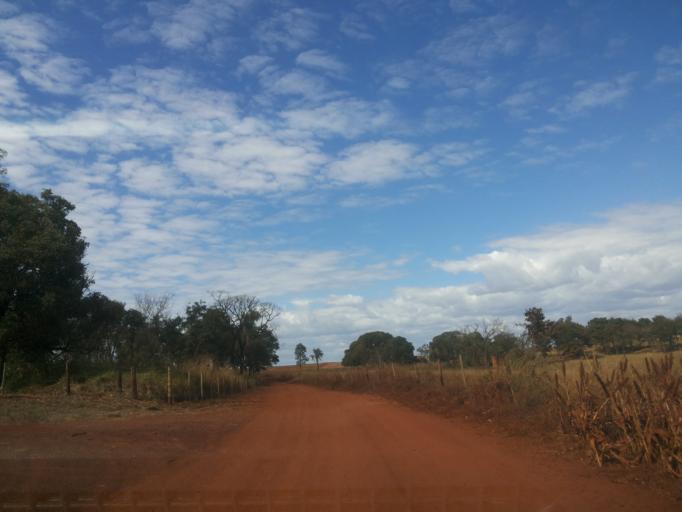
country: BR
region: Minas Gerais
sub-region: Centralina
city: Centralina
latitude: -18.5601
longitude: -49.2286
